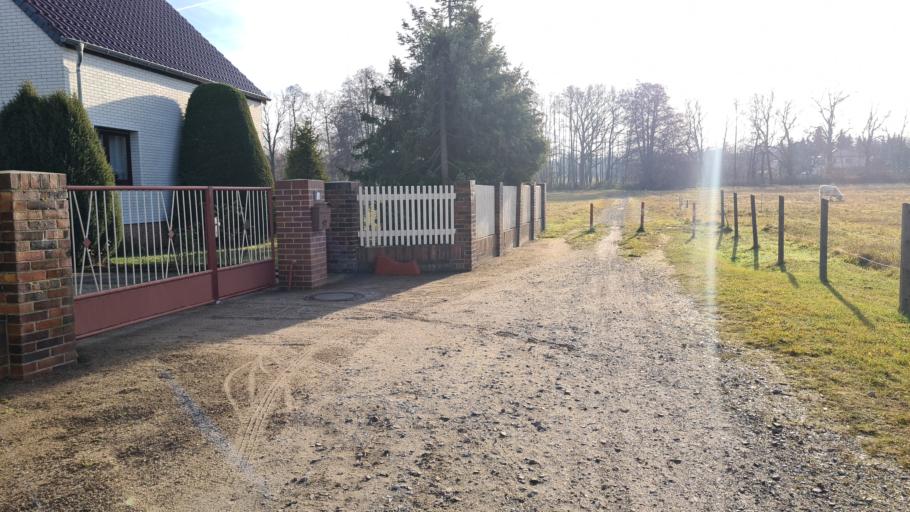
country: DE
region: Brandenburg
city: Doberlug-Kirchhain
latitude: 51.6320
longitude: 13.5726
